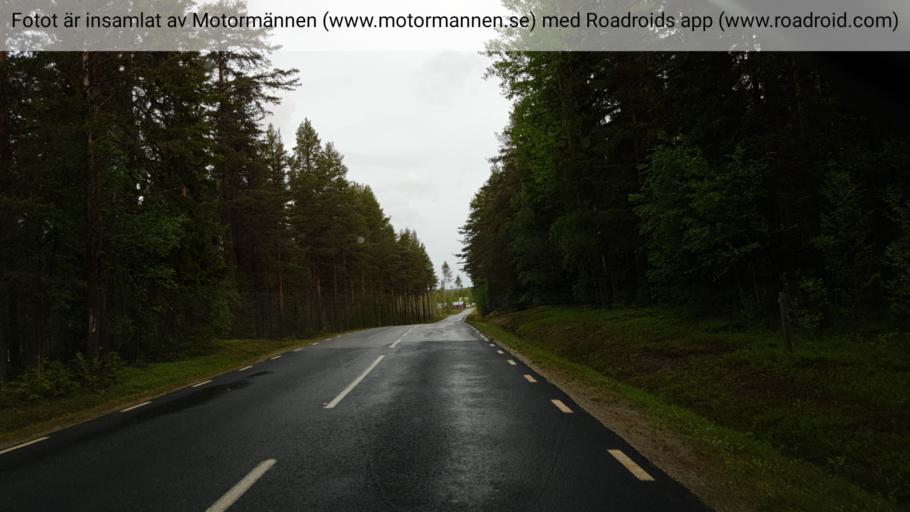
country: SE
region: Vaesterbotten
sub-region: Norsjo Kommun
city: Norsjoe
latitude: 64.6475
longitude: 19.2805
